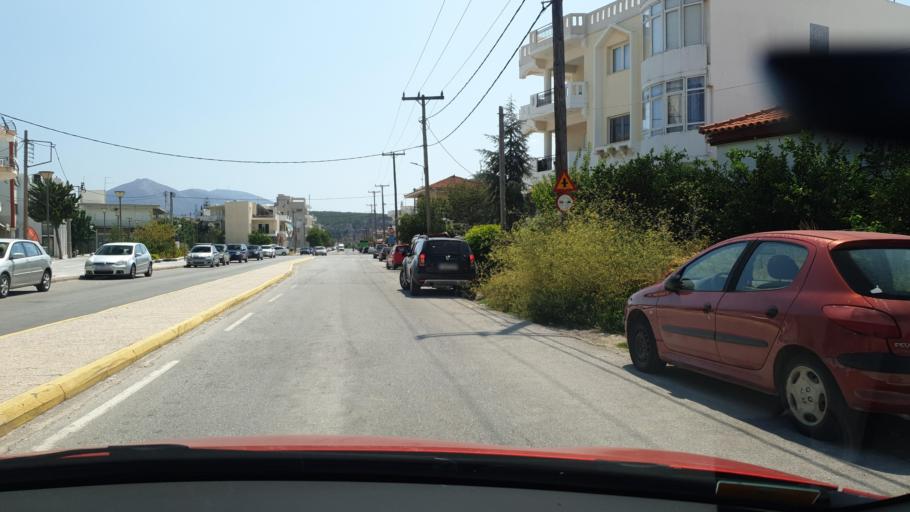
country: GR
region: Central Greece
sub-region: Nomos Evvoias
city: Aliveri
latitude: 38.4094
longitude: 24.0334
